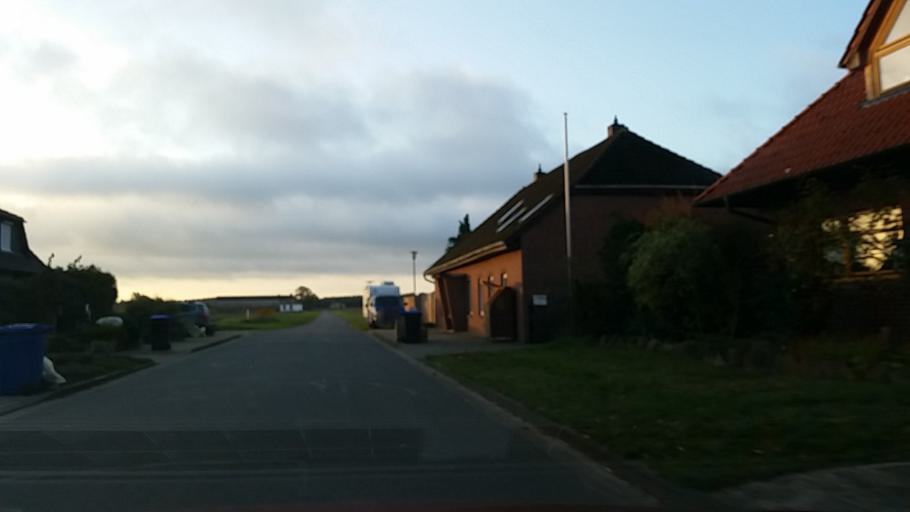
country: DE
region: Lower Saxony
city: Luder
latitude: 52.8095
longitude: 10.6713
